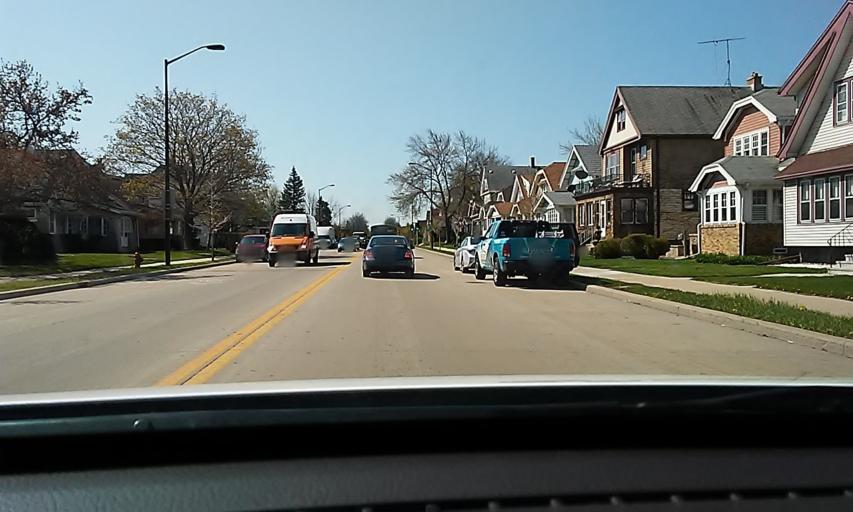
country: US
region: Wisconsin
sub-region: Milwaukee County
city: West Milwaukee
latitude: 43.0151
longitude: -87.9874
